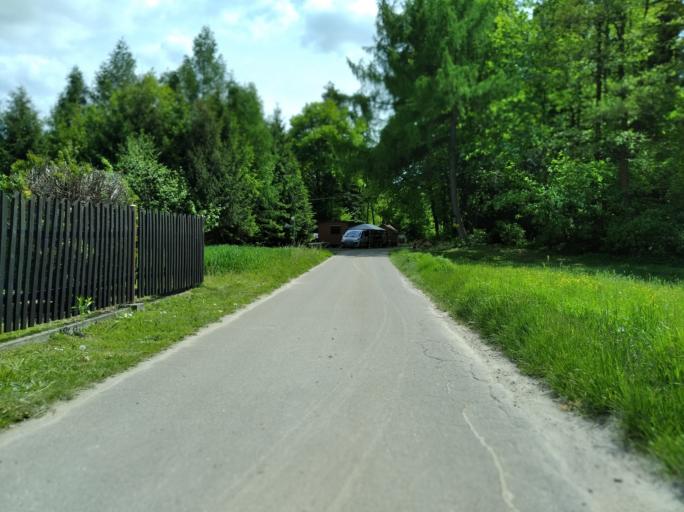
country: PL
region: Subcarpathian Voivodeship
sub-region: Powiat strzyzowski
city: Wisniowa
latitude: 49.8842
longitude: 21.6342
